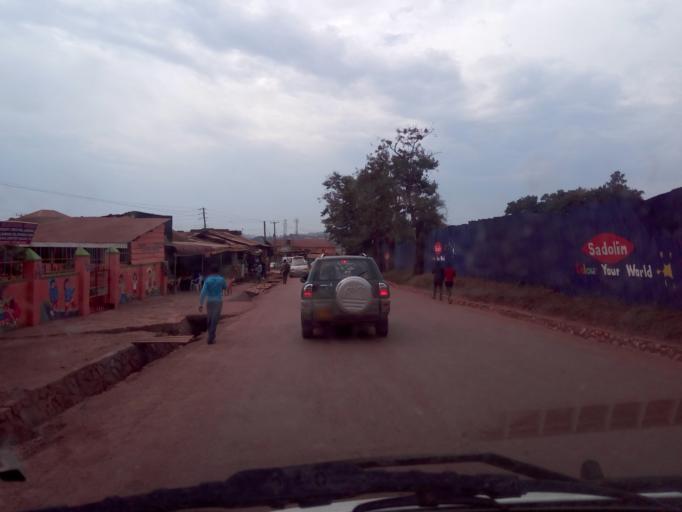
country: UG
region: Central Region
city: Kampala Central Division
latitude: 0.3438
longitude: 32.5769
